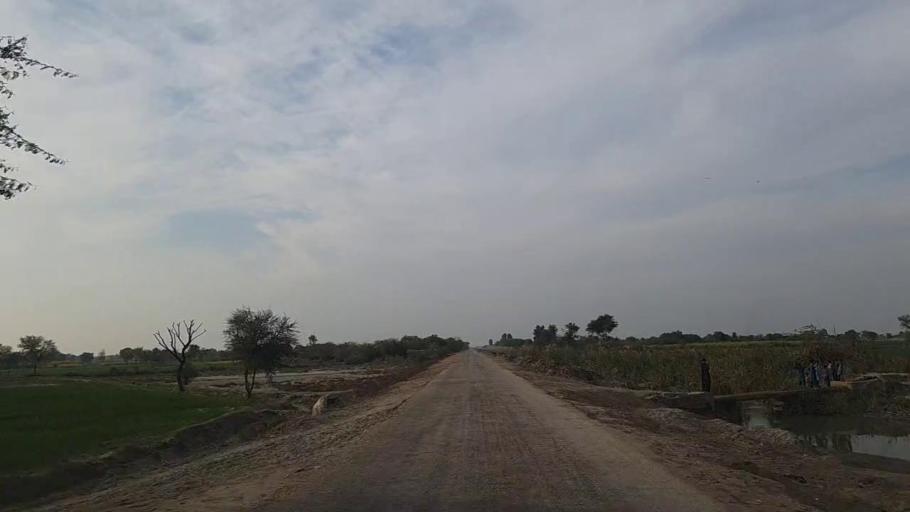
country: PK
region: Sindh
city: Daur
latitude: 26.4921
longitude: 68.4568
